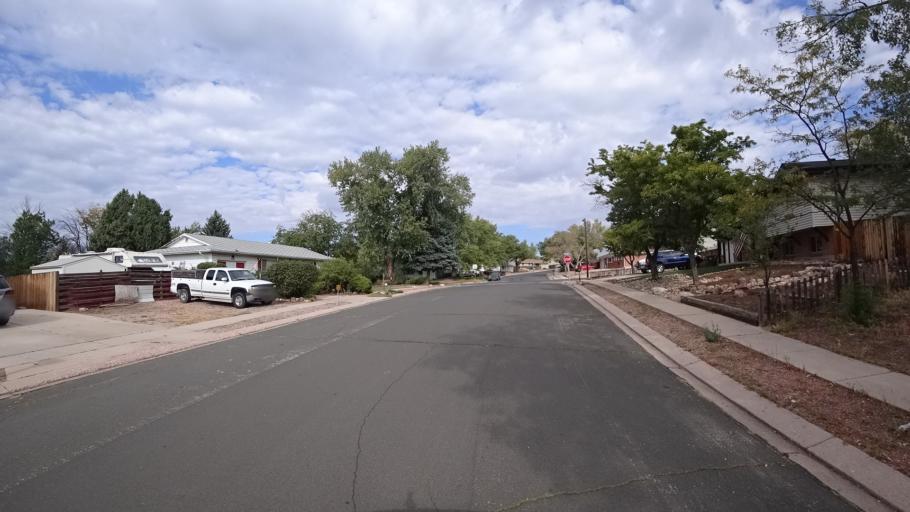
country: US
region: Colorado
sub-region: El Paso County
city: Cimarron Hills
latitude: 38.8406
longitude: -104.7511
